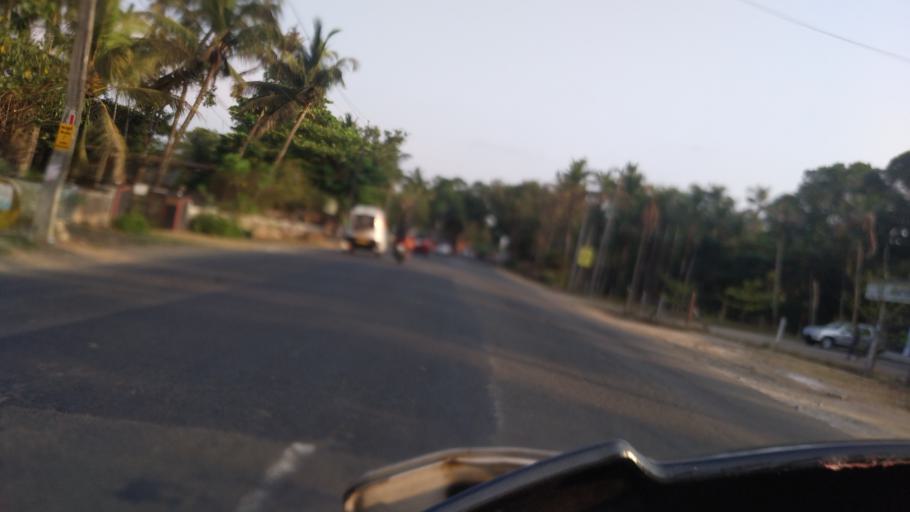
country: IN
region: Kerala
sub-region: Thrissur District
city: Thanniyam
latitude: 10.3822
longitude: 76.1209
